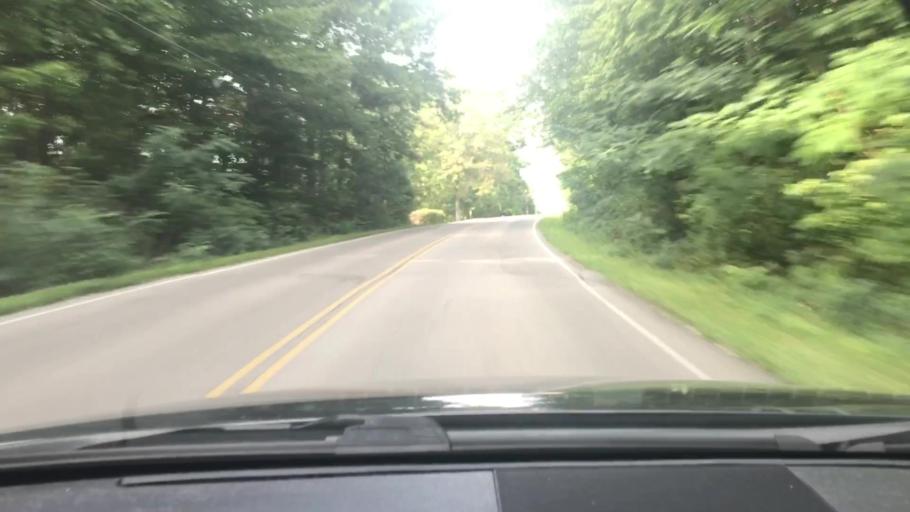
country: US
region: Tennessee
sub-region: Dickson County
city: White Bluff
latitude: 36.0730
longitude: -87.2226
